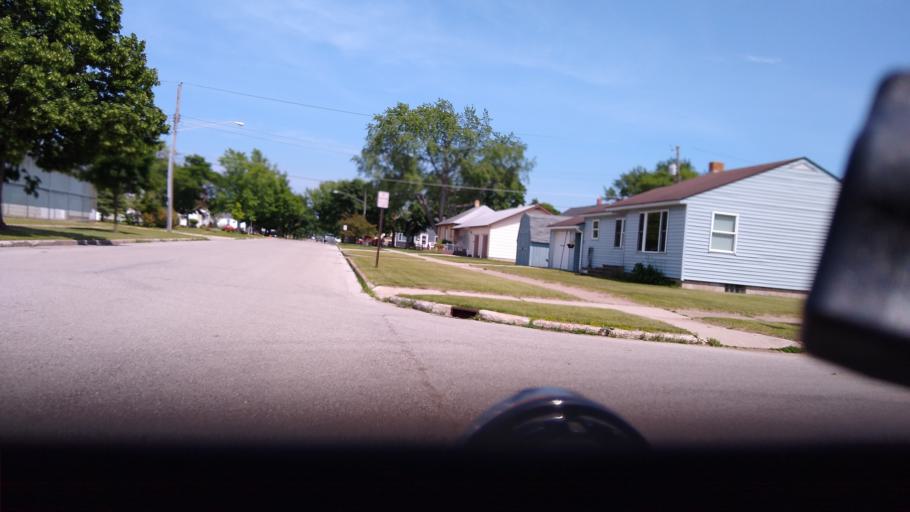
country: US
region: Michigan
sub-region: Delta County
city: Escanaba
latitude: 45.7372
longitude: -87.0727
